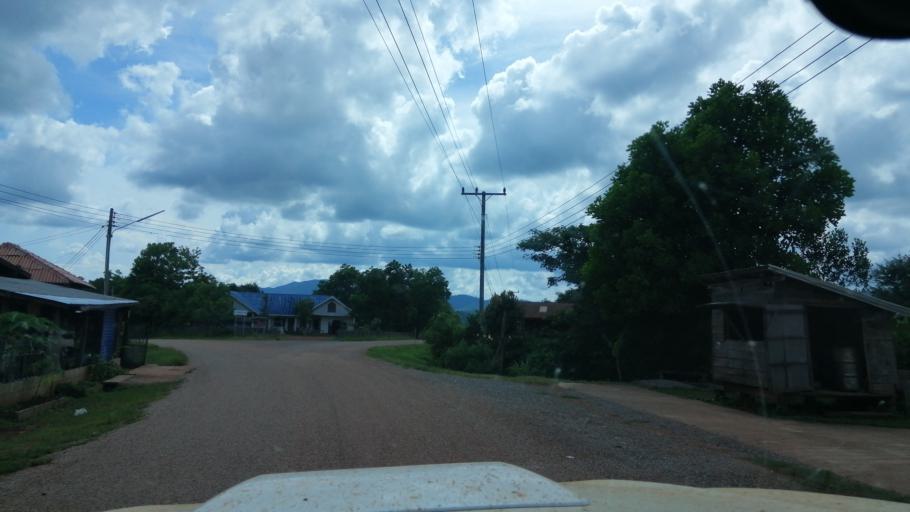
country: TH
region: Uttaradit
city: Ban Khok
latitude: 18.3648
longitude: 101.1403
